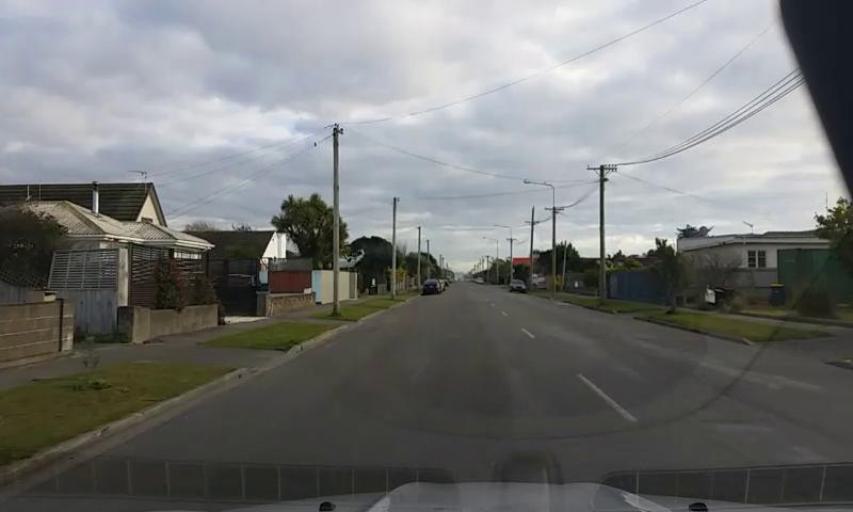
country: NZ
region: Canterbury
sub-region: Christchurch City
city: Christchurch
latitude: -43.5335
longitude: 172.7371
